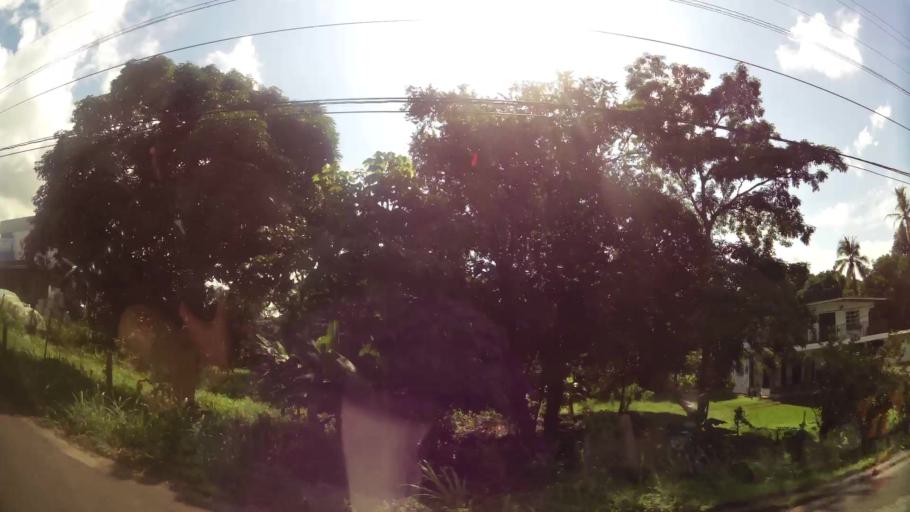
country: PA
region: Panama
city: Nuevo Arraijan
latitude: 8.9086
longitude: -79.7457
